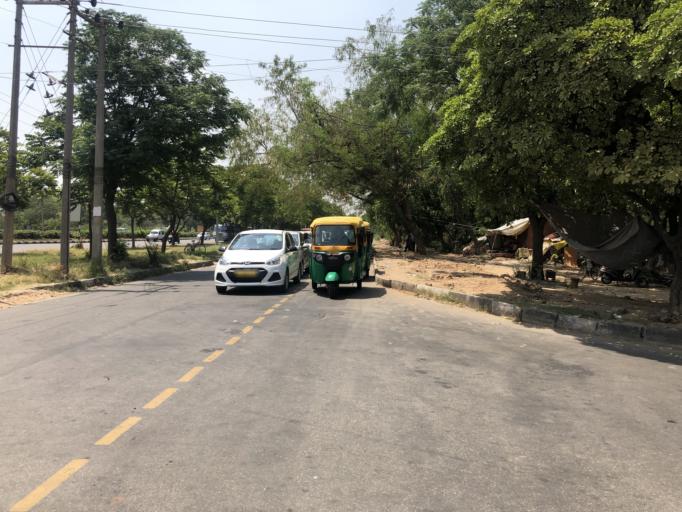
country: IN
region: Punjab
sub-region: Ajitgarh
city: Mohali
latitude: 30.7098
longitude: 76.7484
